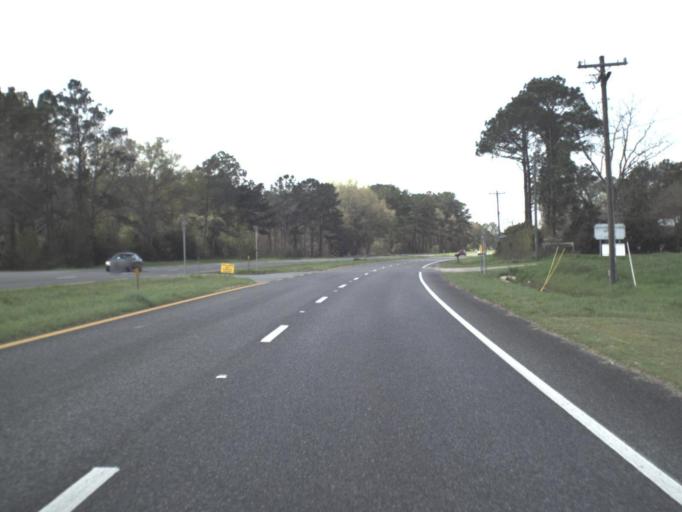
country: US
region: Florida
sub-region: Gadsden County
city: Havana
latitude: 30.6757
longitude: -84.3877
